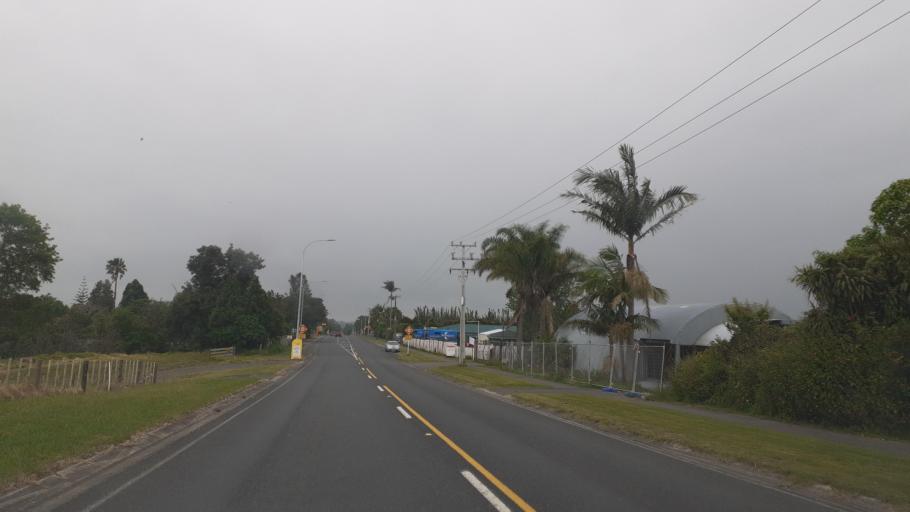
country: NZ
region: Northland
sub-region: Far North District
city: Kerikeri
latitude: -35.2363
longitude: 173.9412
